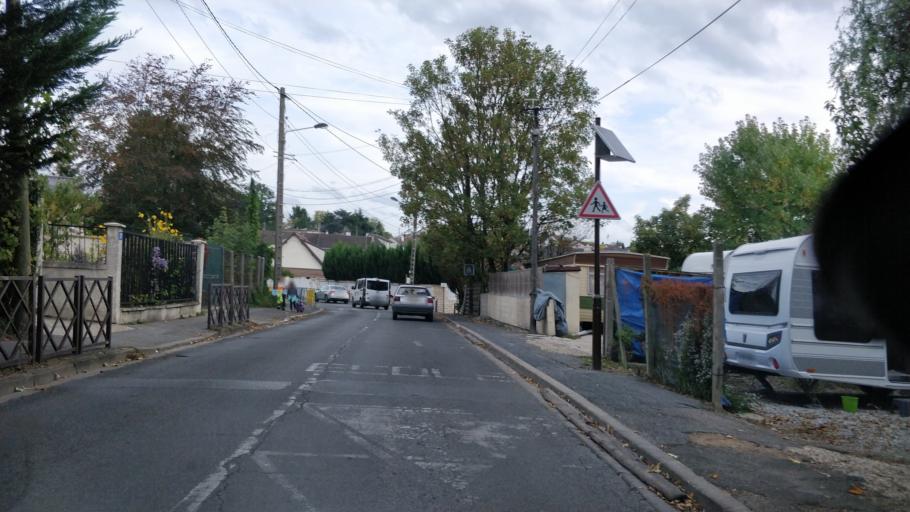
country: FR
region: Ile-de-France
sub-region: Departement de Seine-Saint-Denis
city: Livry-Gargan
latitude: 48.9171
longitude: 2.5459
